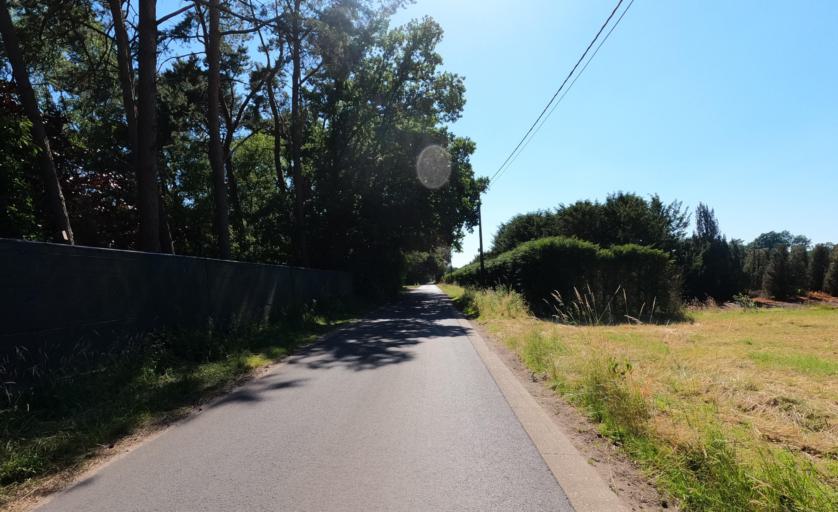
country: BE
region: Flanders
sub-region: Provincie Antwerpen
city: Beerse
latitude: 51.2940
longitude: 4.8432
